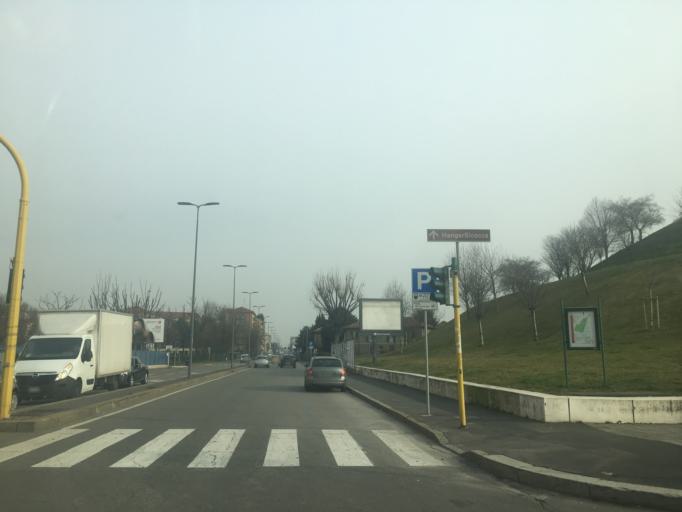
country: IT
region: Lombardy
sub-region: Citta metropolitana di Milano
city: Bresso
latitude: 45.5109
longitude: 9.2061
